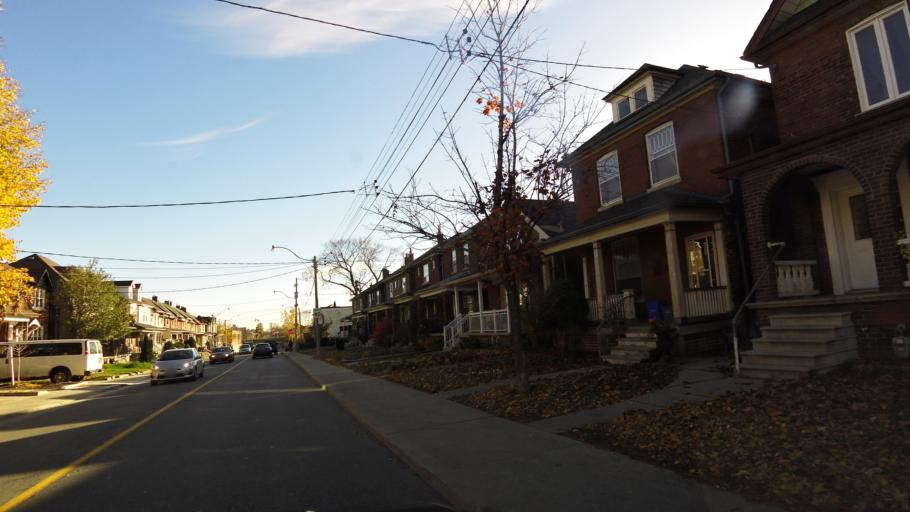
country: CA
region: Ontario
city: Toronto
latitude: 43.6692
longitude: -79.4527
